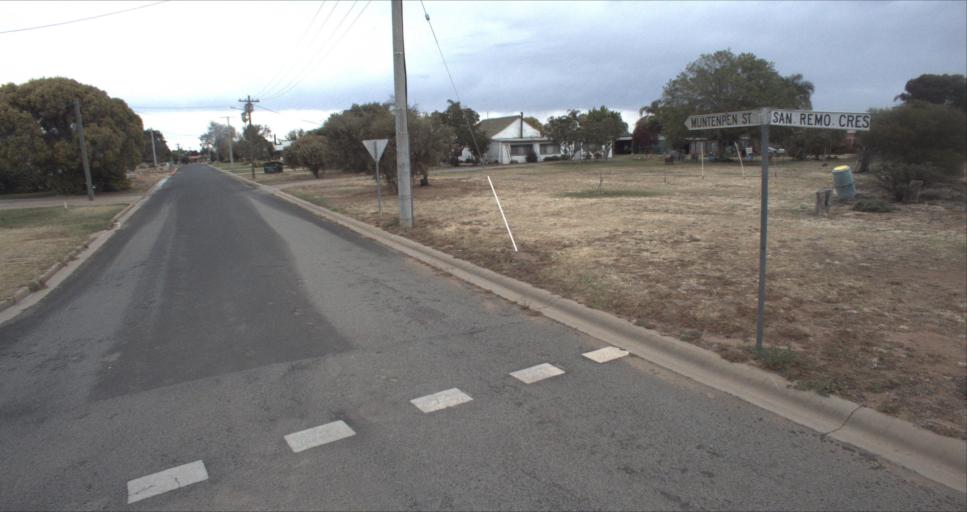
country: AU
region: New South Wales
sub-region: Leeton
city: Leeton
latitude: -34.5433
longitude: 146.4016
